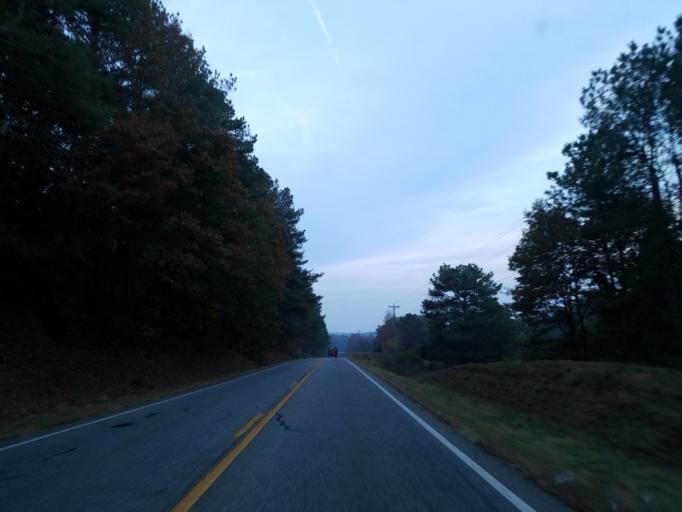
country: US
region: Georgia
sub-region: Gilmer County
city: Ellijay
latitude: 34.5758
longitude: -84.6154
